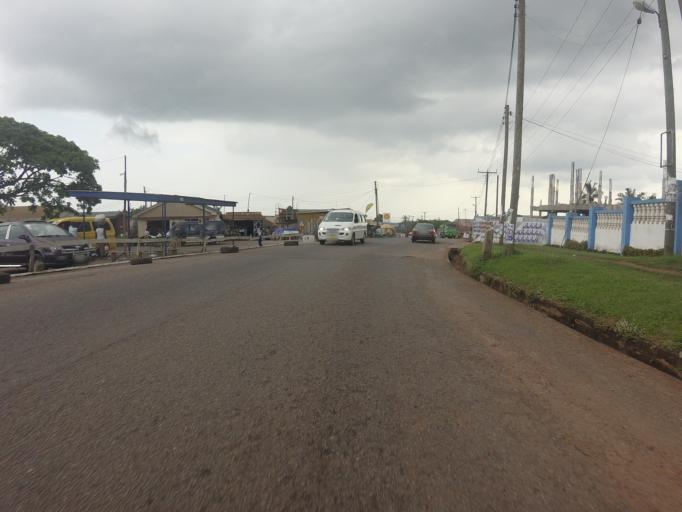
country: GH
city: Akropong
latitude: 5.9402
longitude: -0.1165
